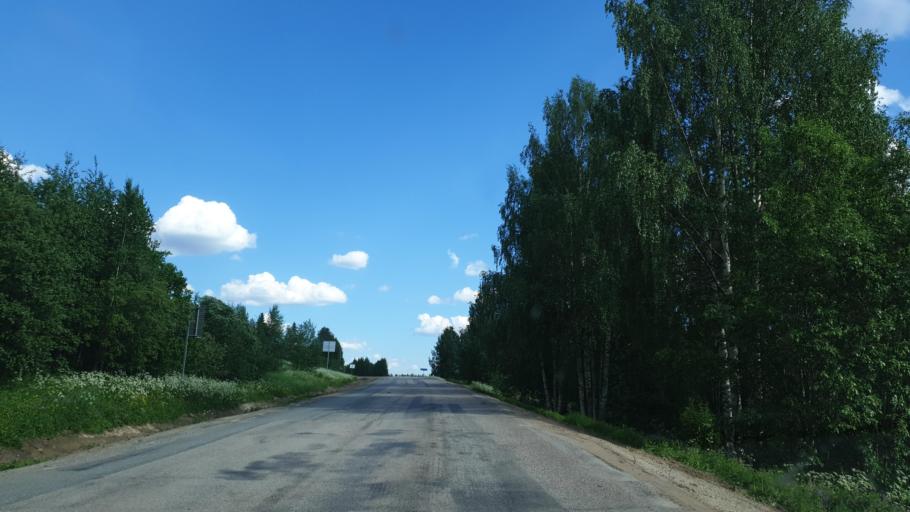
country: SE
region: Norrbotten
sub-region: Alvsbyns Kommun
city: AElvsbyn
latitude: 65.8548
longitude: 20.4332
